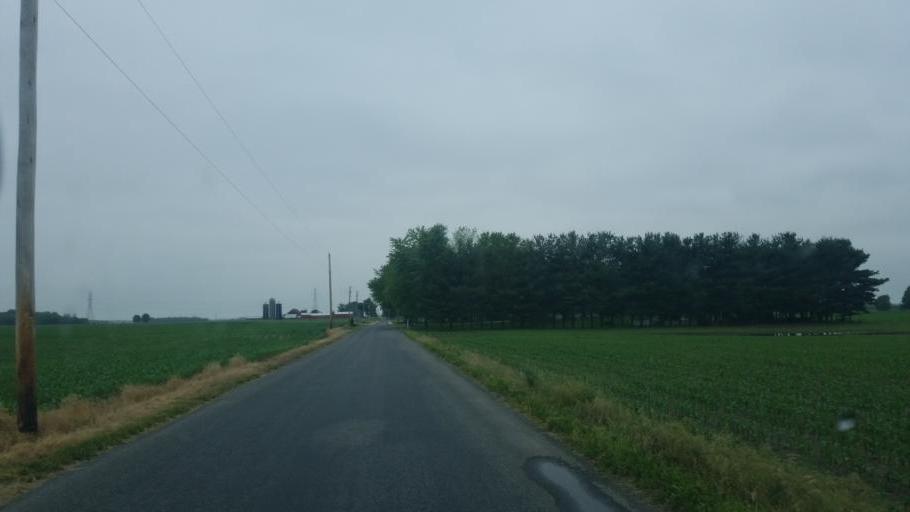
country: US
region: Indiana
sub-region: Marshall County
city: Bremen
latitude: 41.4938
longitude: -86.1300
